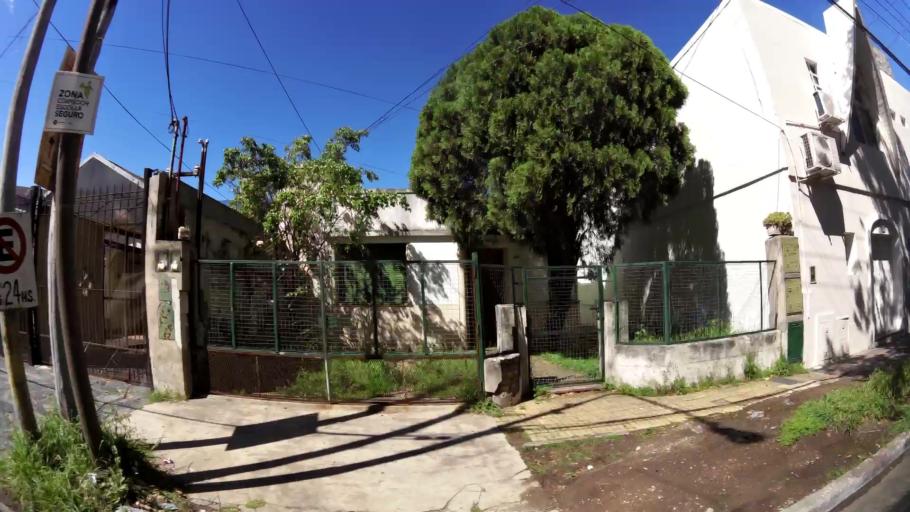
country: AR
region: Buenos Aires
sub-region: Partido de Quilmes
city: Quilmes
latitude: -34.7036
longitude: -58.2908
